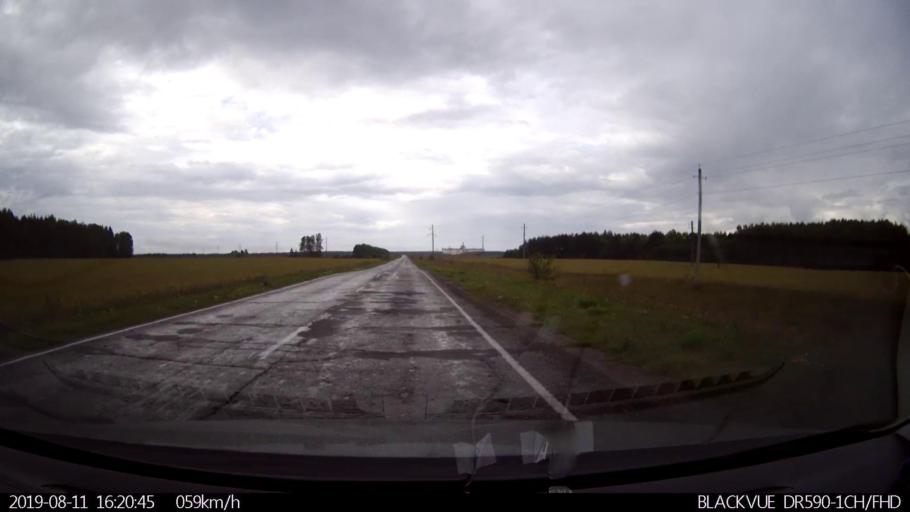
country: RU
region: Ulyanovsk
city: Mayna
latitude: 54.0744
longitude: 47.6013
